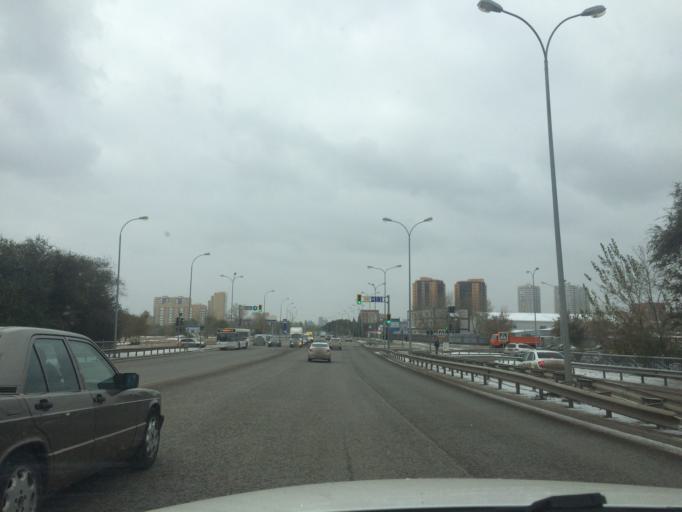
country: KZ
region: Astana Qalasy
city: Astana
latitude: 51.1694
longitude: 71.4791
